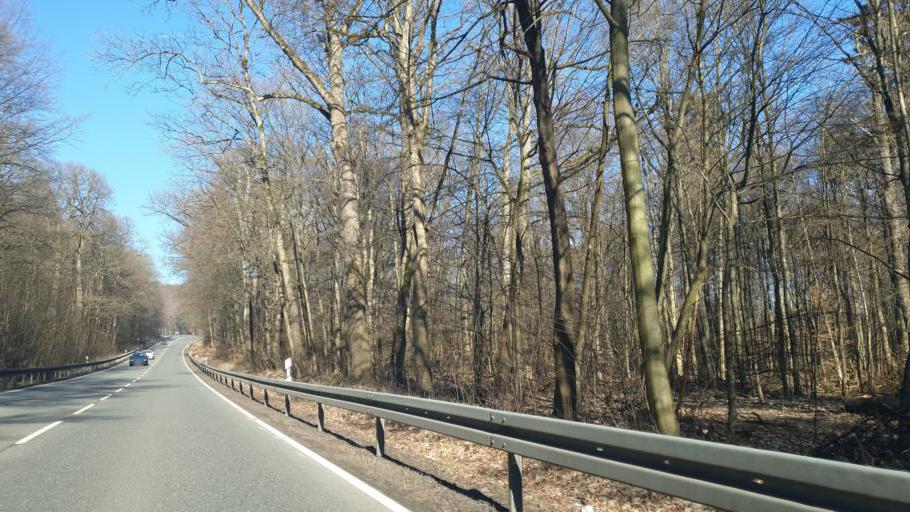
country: DE
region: Hesse
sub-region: Regierungsbezirk Darmstadt
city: Wiesbaden
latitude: 50.1109
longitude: 8.2103
